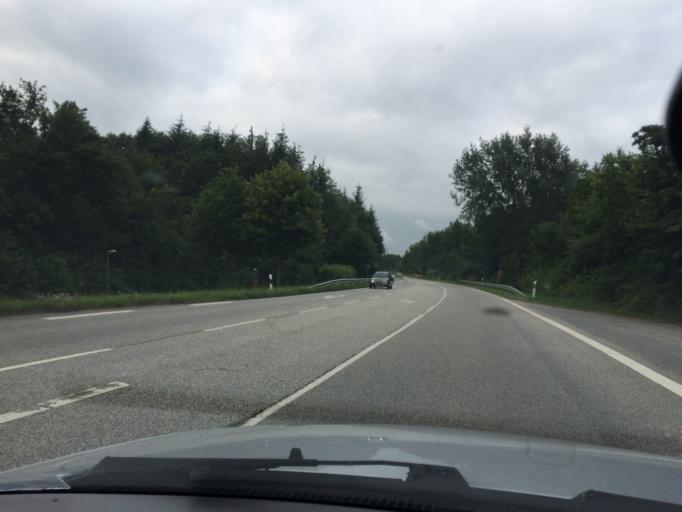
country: DE
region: Schleswig-Holstein
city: Oeversee
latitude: 54.6925
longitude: 9.4316
